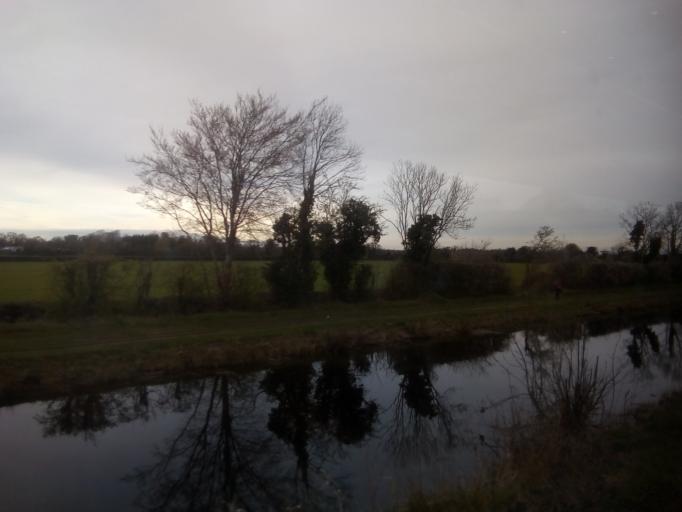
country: IE
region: Leinster
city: Lucan
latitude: 53.3756
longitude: -6.4511
